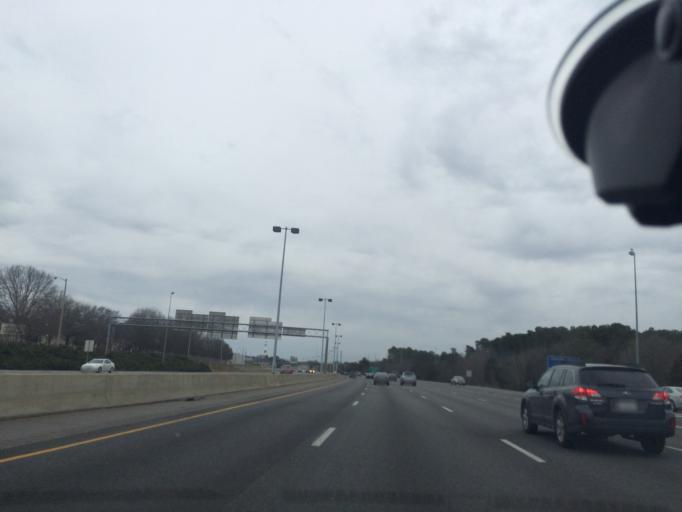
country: US
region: Alabama
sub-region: Madison County
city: Redstone Arsenal
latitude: 34.7190
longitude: -86.6311
